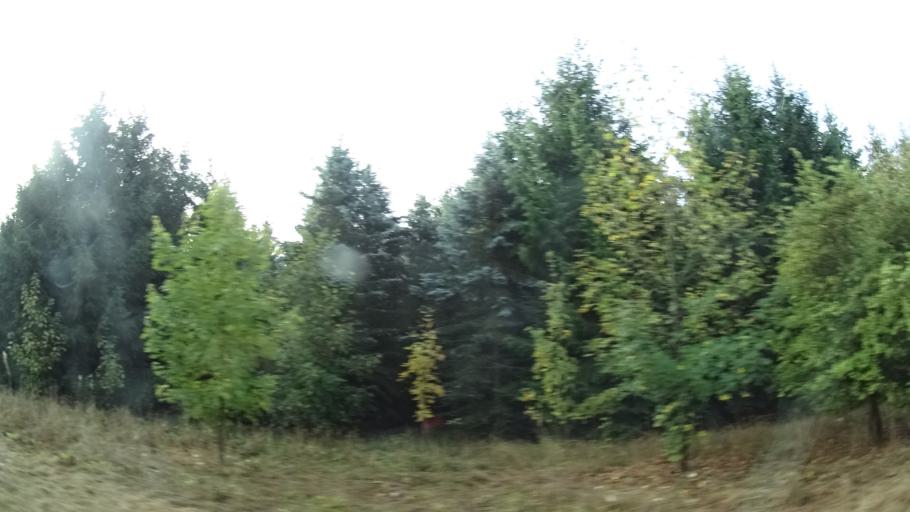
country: DE
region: Hesse
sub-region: Regierungsbezirk Giessen
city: Freiensteinau
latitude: 50.4760
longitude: 9.4288
